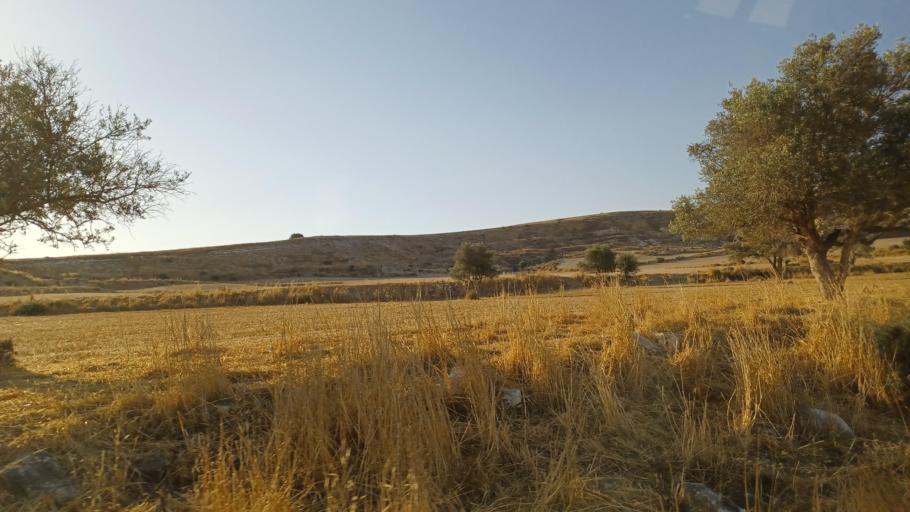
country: CY
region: Larnaka
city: Athienou
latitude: 35.0431
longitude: 33.5210
